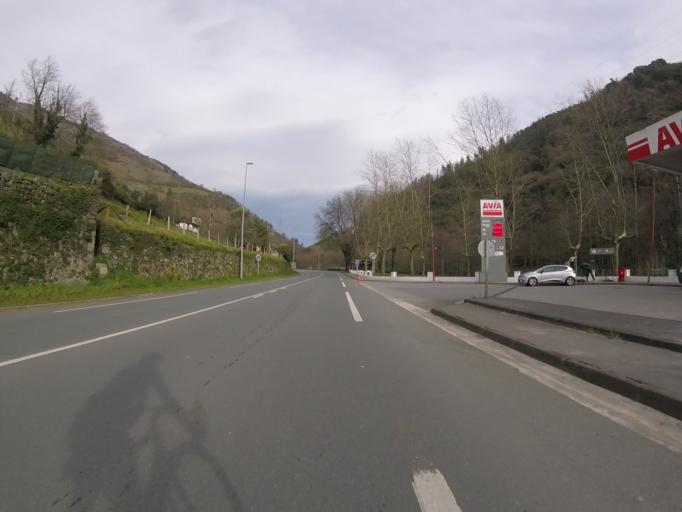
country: ES
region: Basque Country
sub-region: Provincia de Guipuzcoa
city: Azpeitia
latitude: 43.1898
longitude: -2.2590
